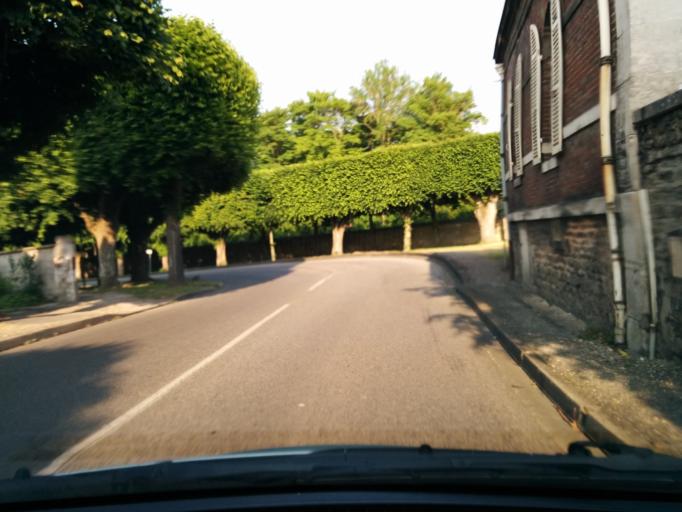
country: FR
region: Haute-Normandie
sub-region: Departement de l'Eure
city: Vernon
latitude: 49.0859
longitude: 1.4641
